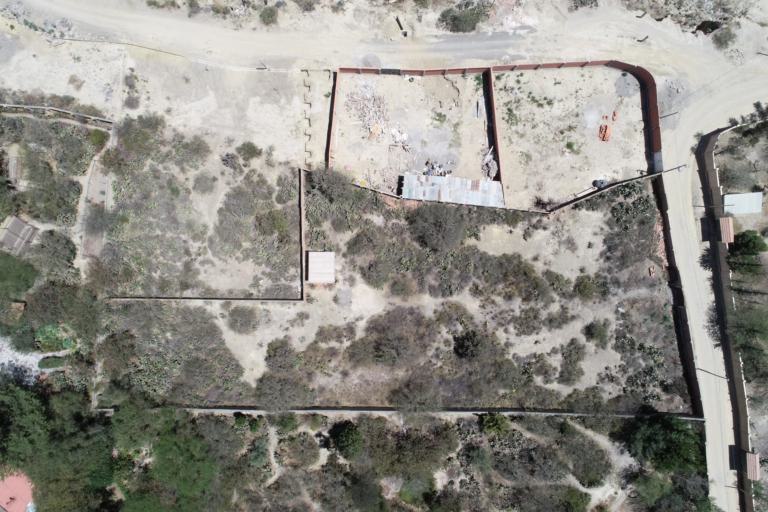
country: BO
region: La Paz
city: La Paz
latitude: -16.6462
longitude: -68.0450
